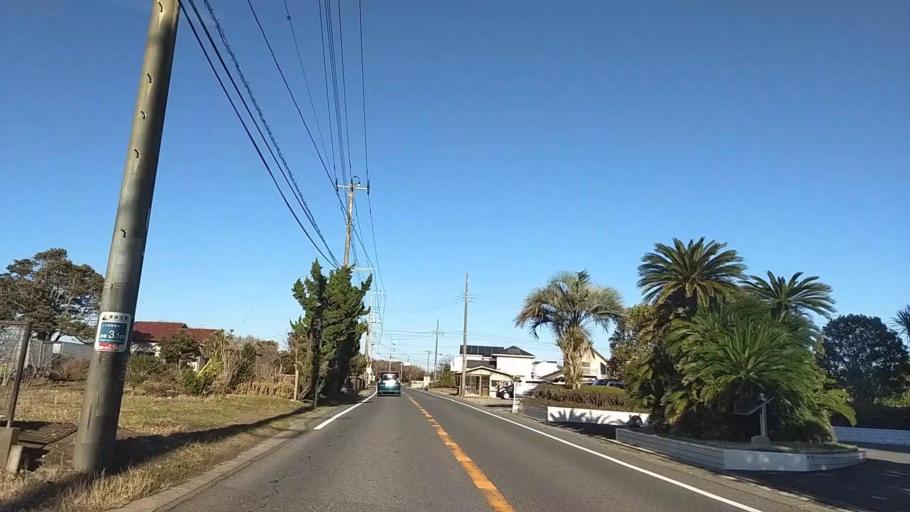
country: JP
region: Chiba
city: Yokaichiba
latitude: 35.6303
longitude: 140.5544
